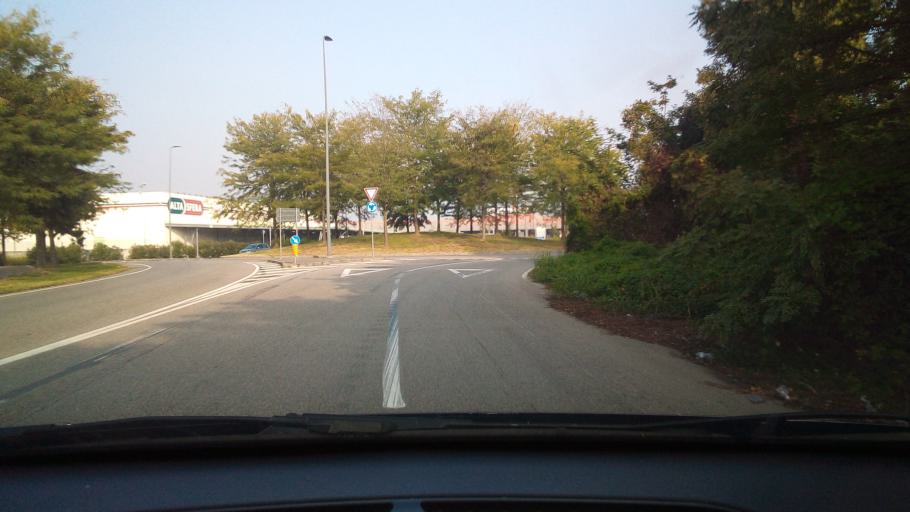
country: IT
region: Lombardy
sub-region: Citta metropolitana di Milano
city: Novegro-Tregarezzo-San Felice
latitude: 45.4833
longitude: 9.2634
